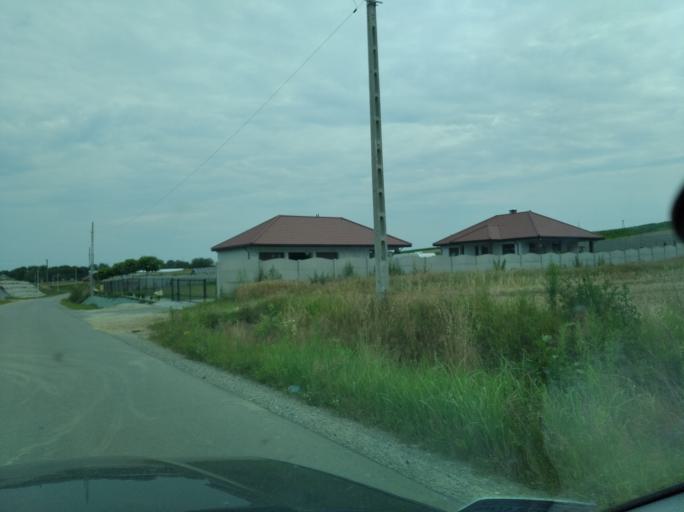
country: PL
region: Subcarpathian Voivodeship
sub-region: Powiat jaroslawski
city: Pawlosiow
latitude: 49.9669
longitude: 22.6281
